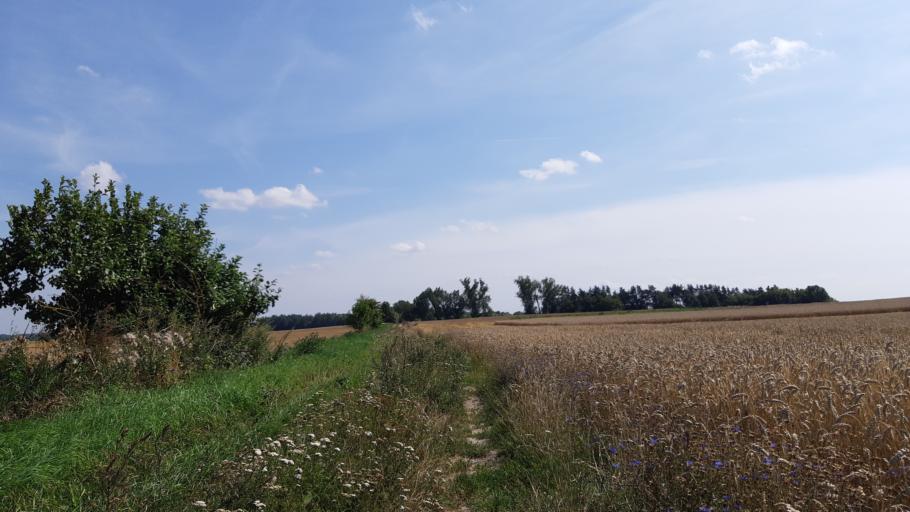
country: LT
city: Virbalis
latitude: 54.6430
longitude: 22.8183
